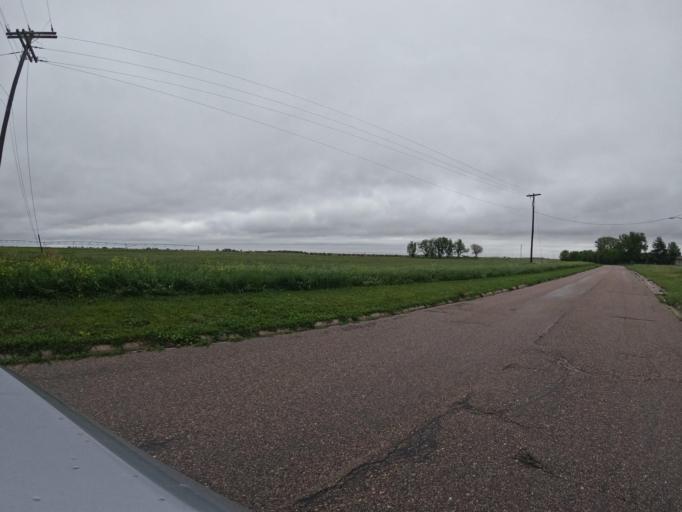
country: US
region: Nebraska
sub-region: Clay County
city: Harvard
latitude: 40.6289
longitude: -98.0915
